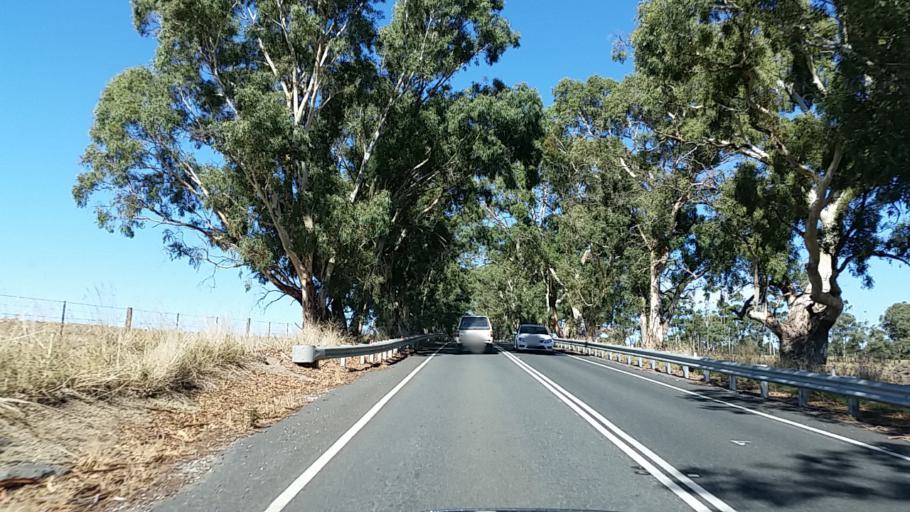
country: AU
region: South Australia
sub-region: Adelaide Hills
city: Birdwood
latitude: -34.7544
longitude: 138.9989
